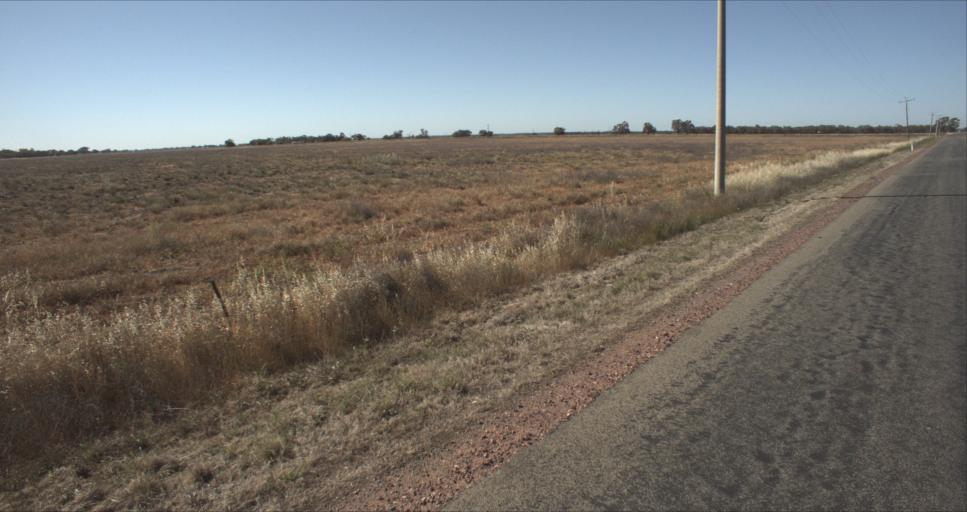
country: AU
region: New South Wales
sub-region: Leeton
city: Leeton
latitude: -34.5513
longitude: 146.2673
